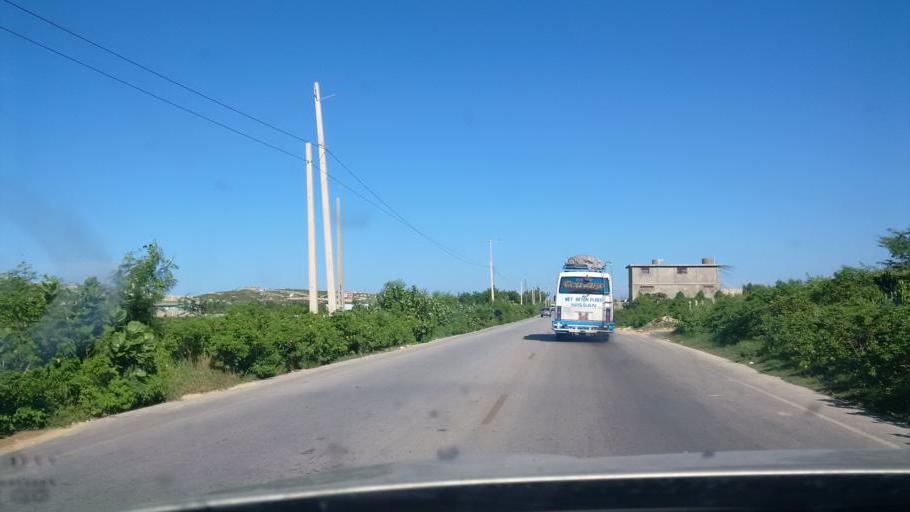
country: HT
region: Ouest
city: Cabaret
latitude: 18.7251
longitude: -72.3839
